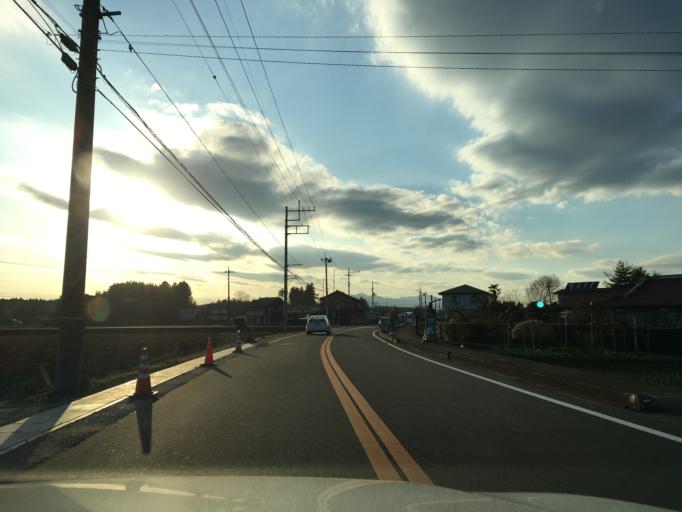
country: JP
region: Tochigi
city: Otawara
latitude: 36.8579
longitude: 140.1028
